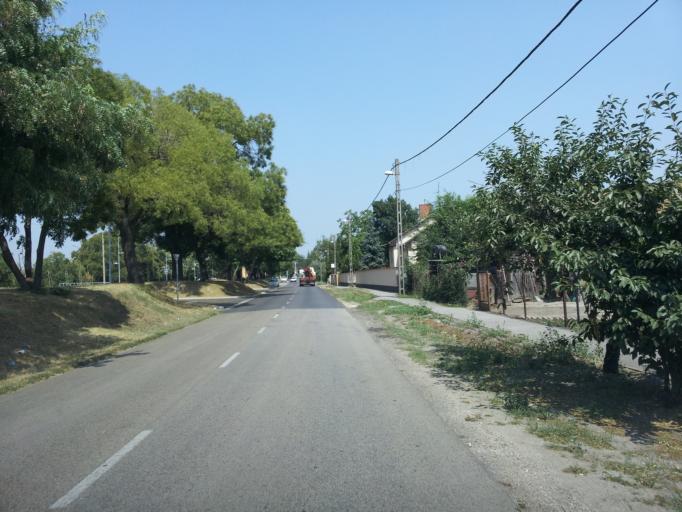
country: HU
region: Pest
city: Dunavarsany
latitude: 47.2723
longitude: 19.0649
